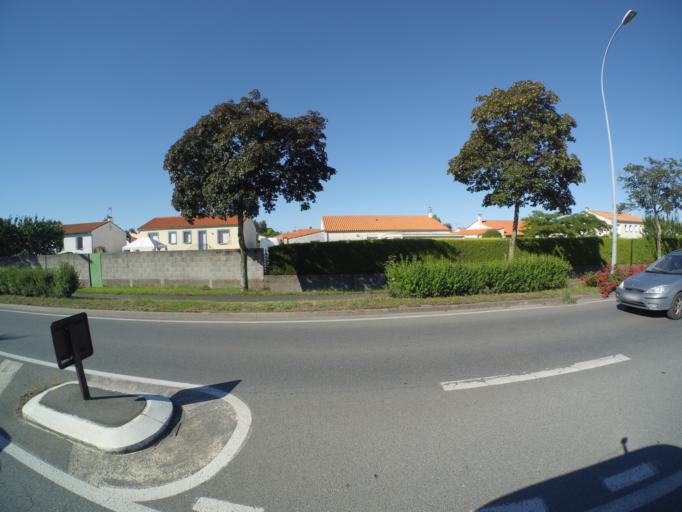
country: FR
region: Pays de la Loire
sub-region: Departement de la Vendee
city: Les Herbiers
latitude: 46.8590
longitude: -1.0153
